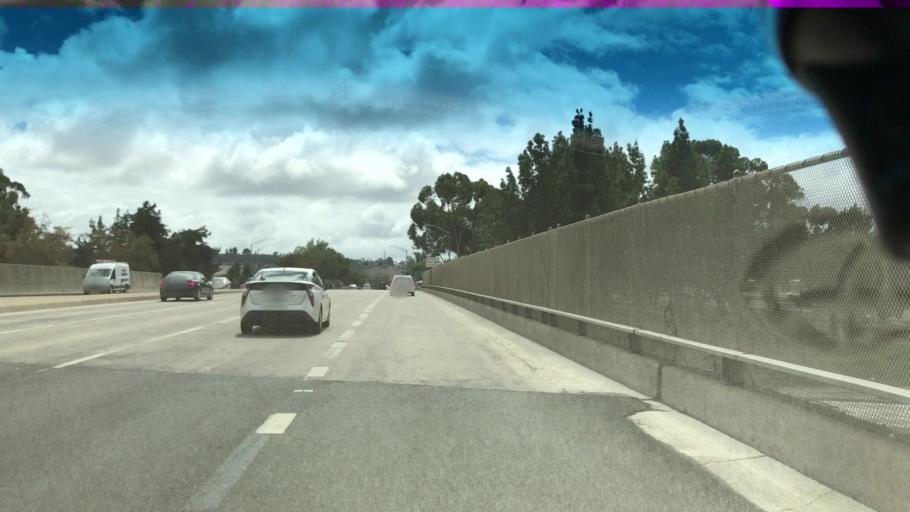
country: US
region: California
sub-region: Orange County
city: Mission Viejo
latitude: 33.6051
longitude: -117.6905
